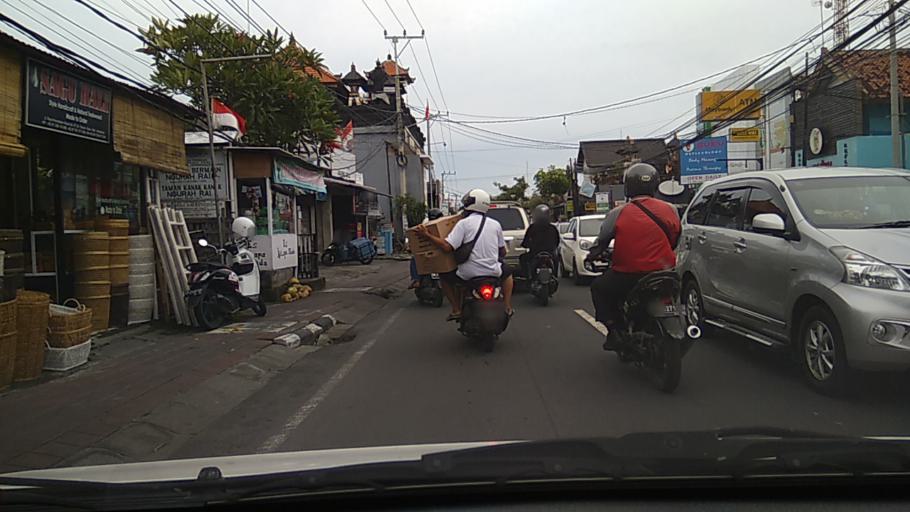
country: ID
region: Bali
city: Kuta
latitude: -8.6763
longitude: 115.1648
